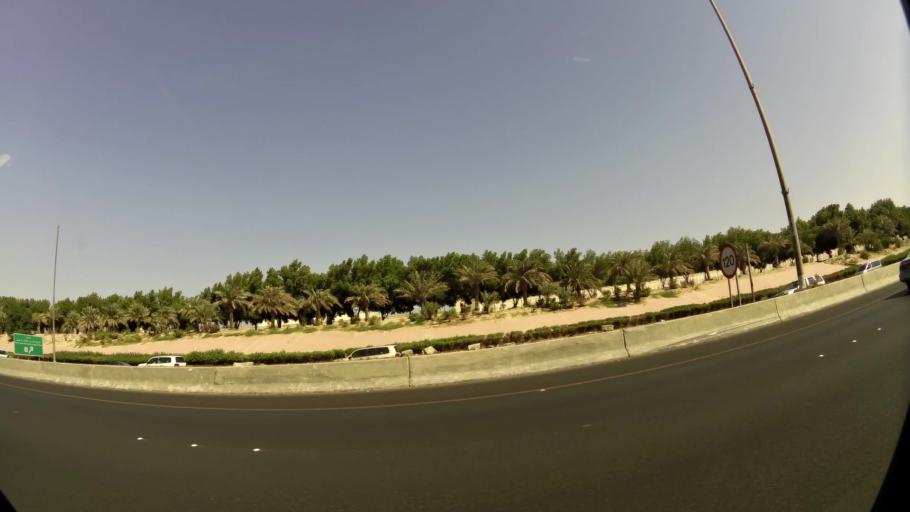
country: KW
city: Bayan
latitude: 29.2984
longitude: 48.0257
